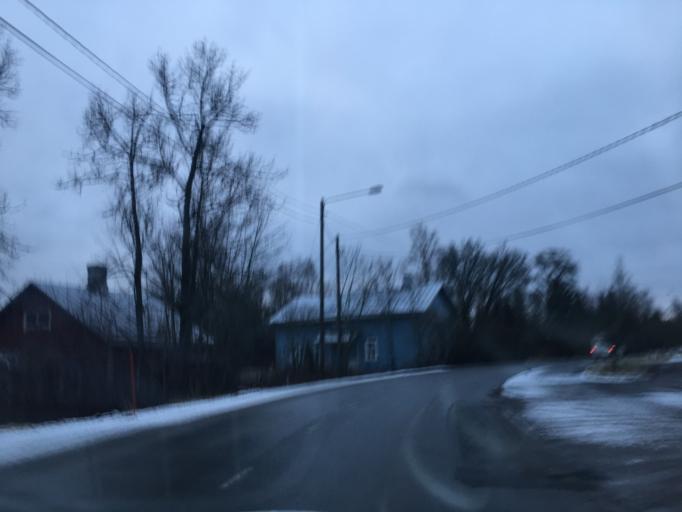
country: FI
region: Varsinais-Suomi
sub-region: Loimaa
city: Aura
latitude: 60.6443
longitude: 22.5919
